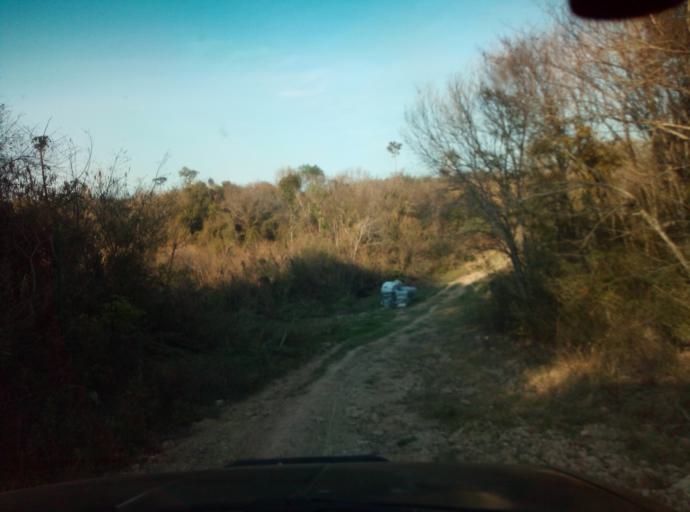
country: PY
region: Caaguazu
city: Doctor Cecilio Baez
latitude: -25.1996
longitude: -56.1202
